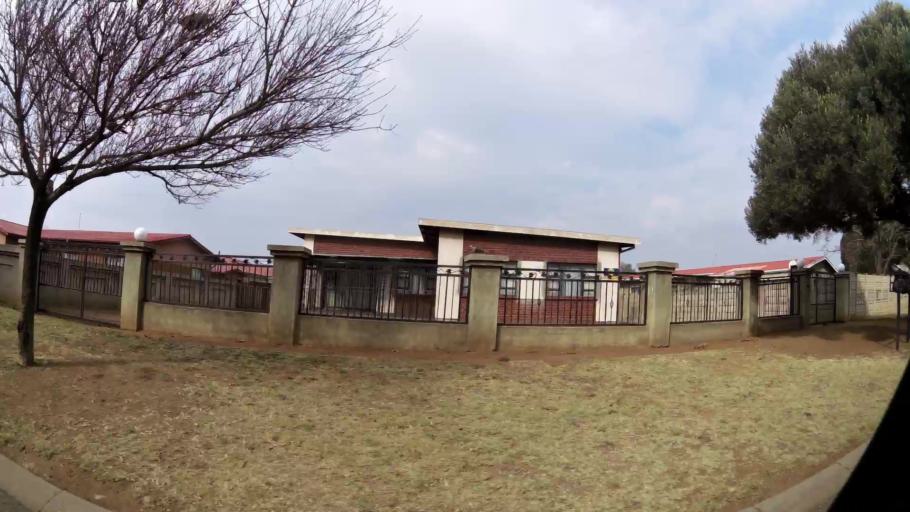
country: ZA
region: Gauteng
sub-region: Sedibeng District Municipality
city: Vanderbijlpark
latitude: -26.6806
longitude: 27.8376
